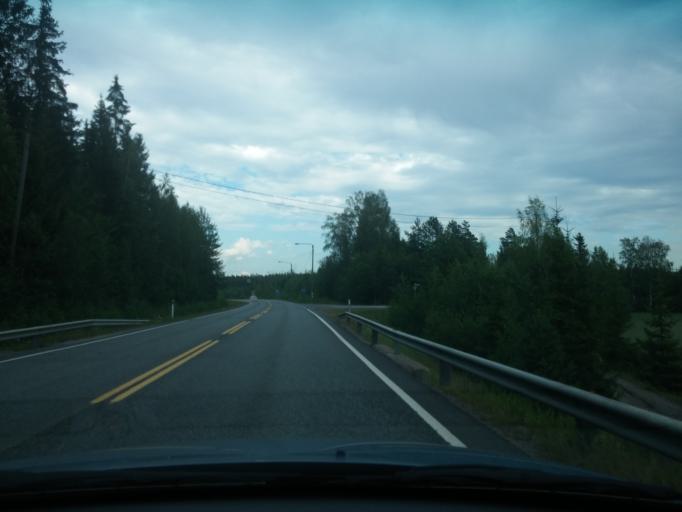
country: FI
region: Haeme
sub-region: Riihimaeki
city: Riihimaeki
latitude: 60.7477
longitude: 24.7126
